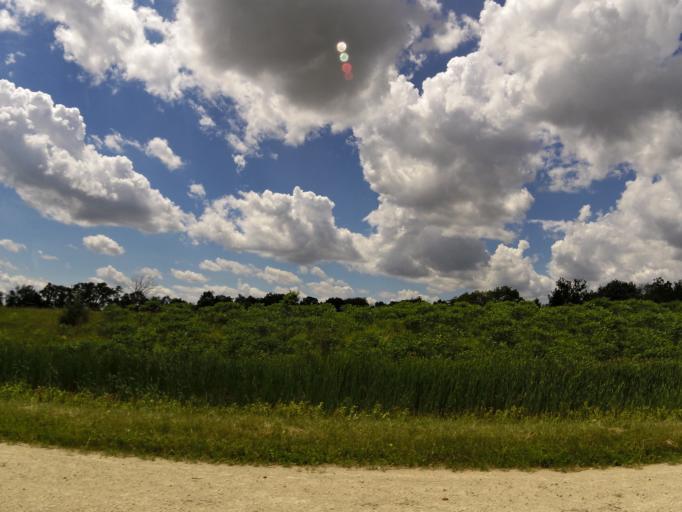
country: US
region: Iowa
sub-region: Fayette County
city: Oelwein
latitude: 42.6002
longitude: -91.9023
